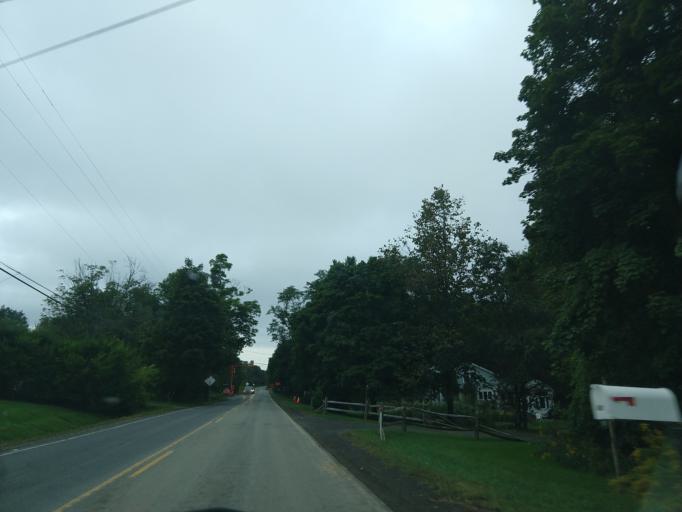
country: US
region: New York
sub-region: Tompkins County
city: East Ithaca
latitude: 42.4042
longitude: -76.4646
